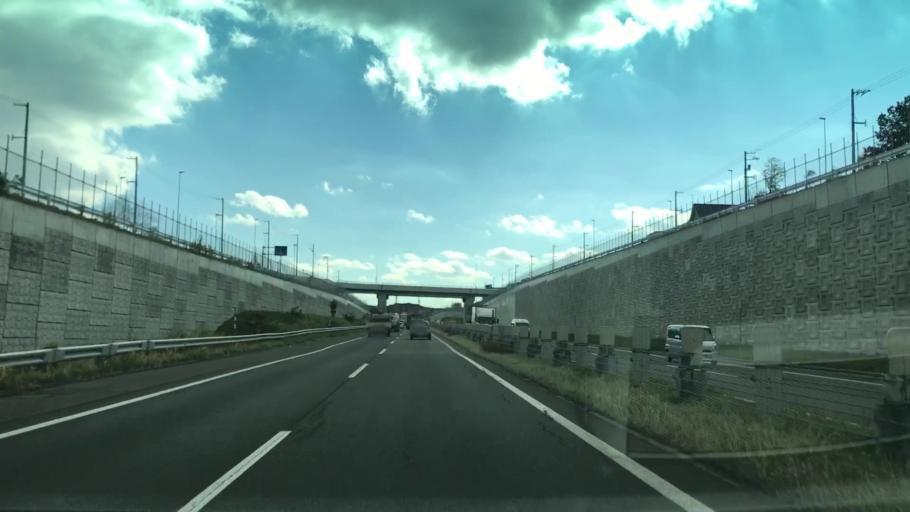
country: JP
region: Hokkaido
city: Kitahiroshima
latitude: 42.9955
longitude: 141.4688
